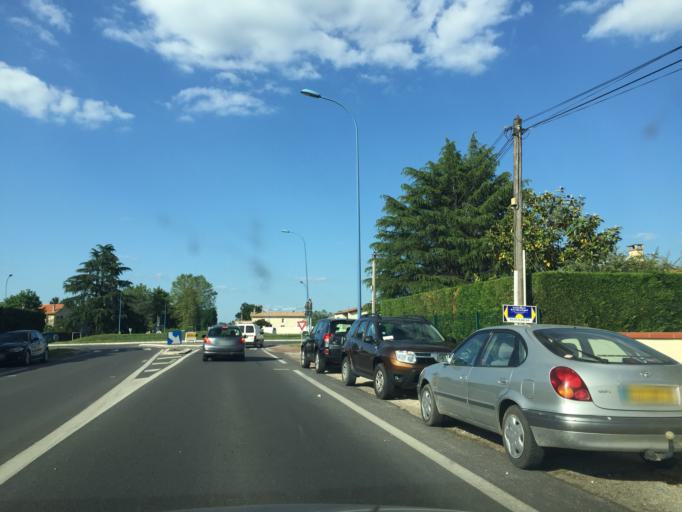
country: FR
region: Aquitaine
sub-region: Departement de la Gironde
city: Saint-Denis-de-Pile
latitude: 44.9894
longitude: -0.2007
